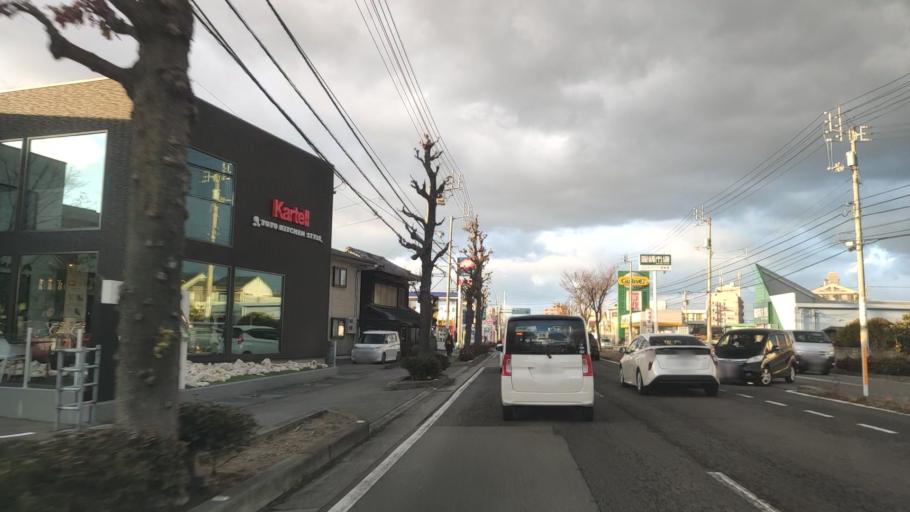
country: JP
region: Ehime
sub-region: Shikoku-chuo Shi
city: Matsuyama
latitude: 33.8077
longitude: 132.7808
